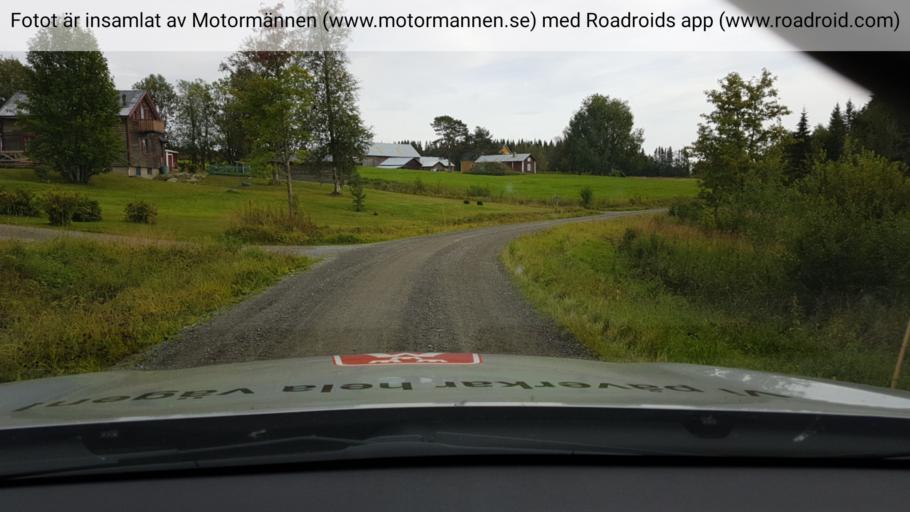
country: SE
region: Jaemtland
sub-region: Krokoms Kommun
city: Valla
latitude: 63.5269
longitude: 13.8849
